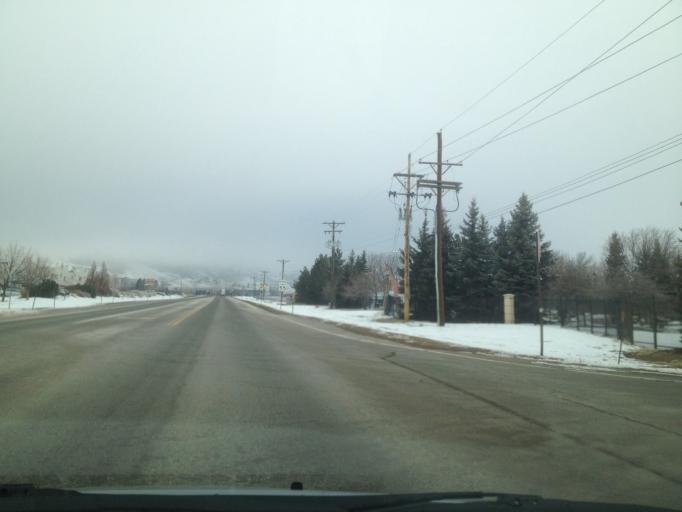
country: US
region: Colorado
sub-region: Boulder County
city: Boulder
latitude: 40.0618
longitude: -105.2766
